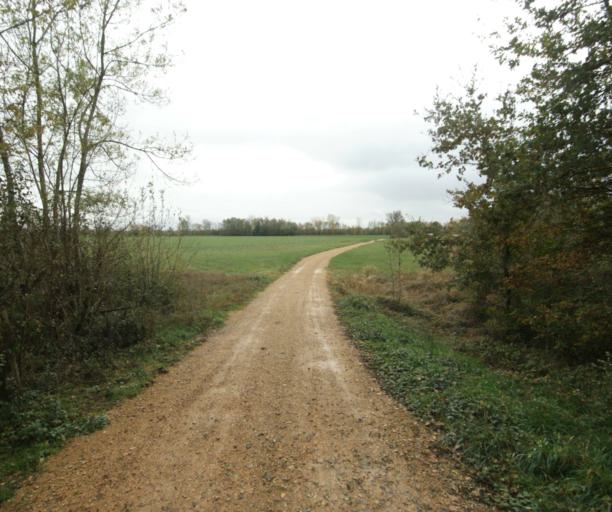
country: FR
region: Rhone-Alpes
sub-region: Departement de l'Ain
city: Pont-de-Vaux
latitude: 46.4585
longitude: 4.9019
